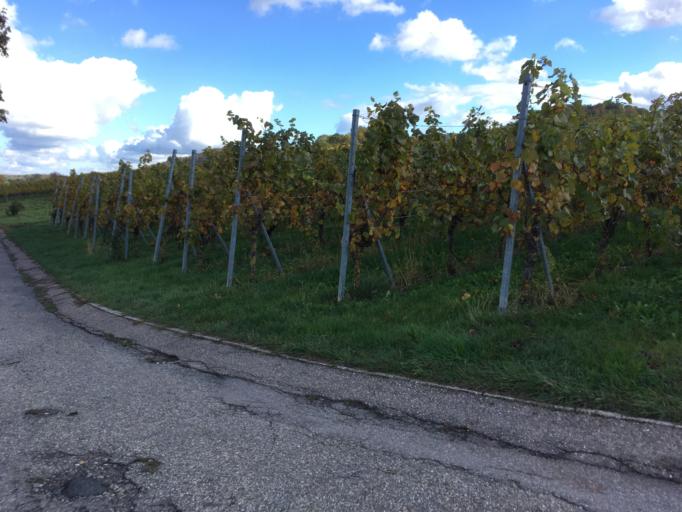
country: DE
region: Baden-Wuerttemberg
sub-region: Regierungsbezirk Stuttgart
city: Neuenstein
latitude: 49.1796
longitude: 9.5676
